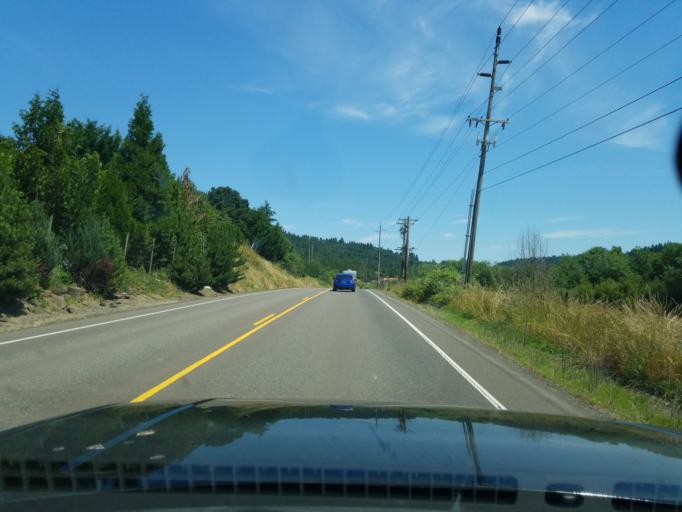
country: US
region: Oregon
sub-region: Yamhill County
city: Yamhill
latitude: 45.3685
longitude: -123.1627
